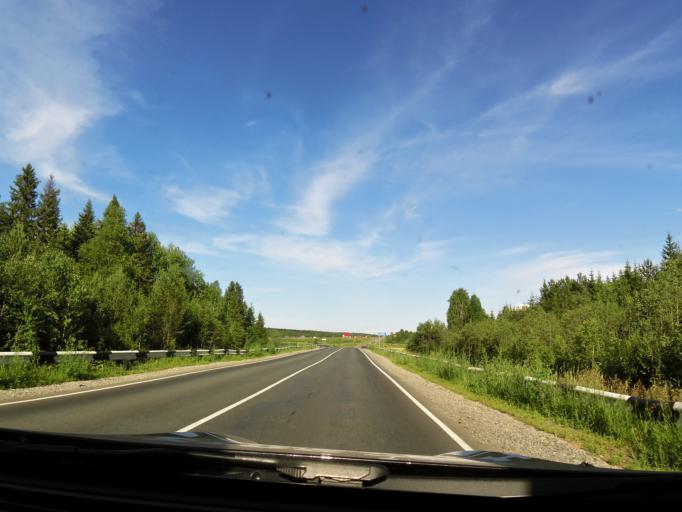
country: RU
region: Kirov
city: Chernaya Kholunitsa
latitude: 58.8590
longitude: 51.6876
